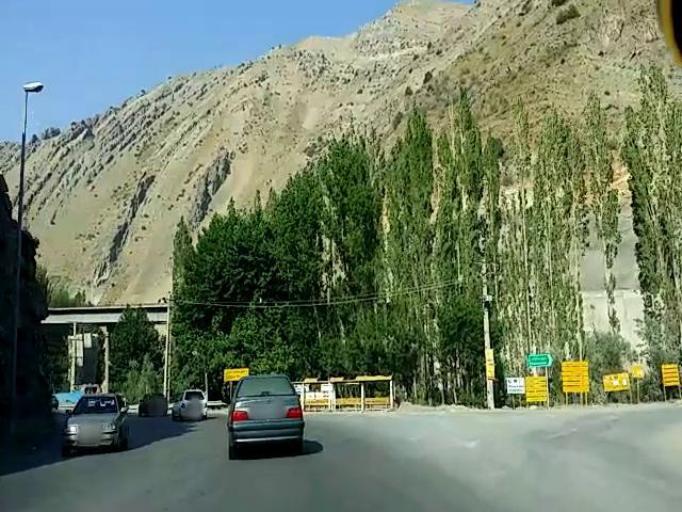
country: IR
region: Tehran
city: Tajrish
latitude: 36.0162
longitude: 51.2981
